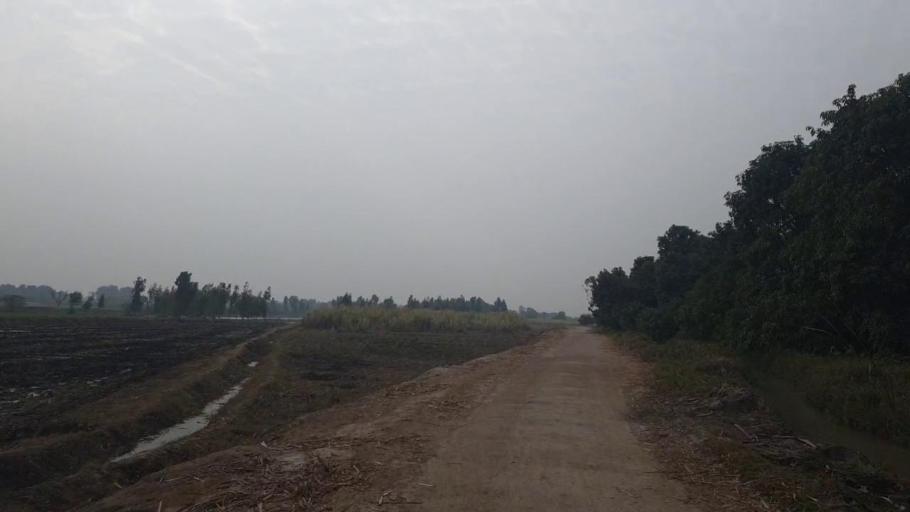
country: PK
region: Sindh
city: Tando Adam
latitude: 25.7171
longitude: 68.7016
